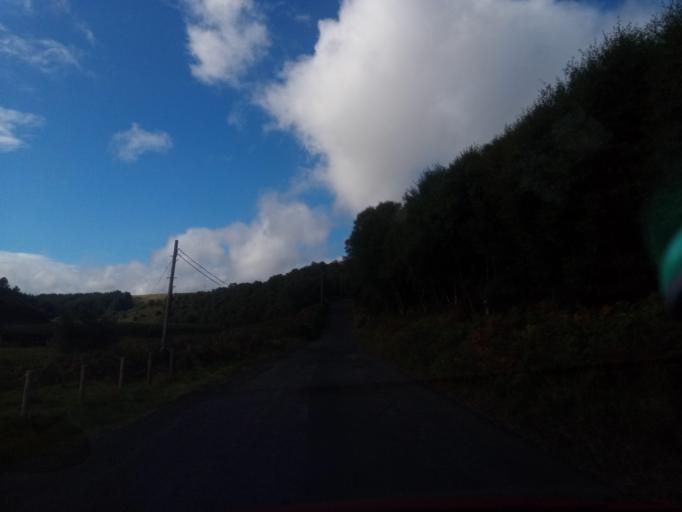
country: GB
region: Scotland
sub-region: East Lothian
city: Dunbar
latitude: 55.8622
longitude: -2.5363
